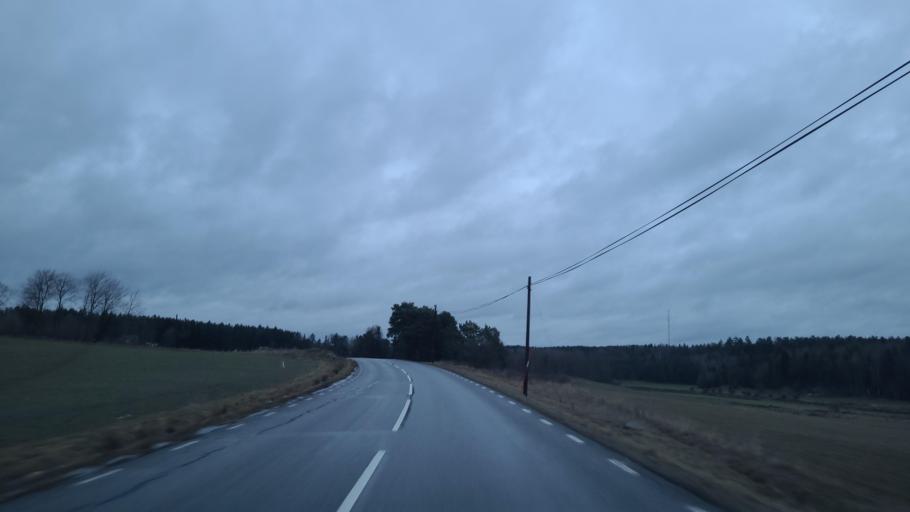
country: SE
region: Stockholm
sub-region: Osterakers Kommun
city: Akersberga
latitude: 59.6158
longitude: 18.3283
